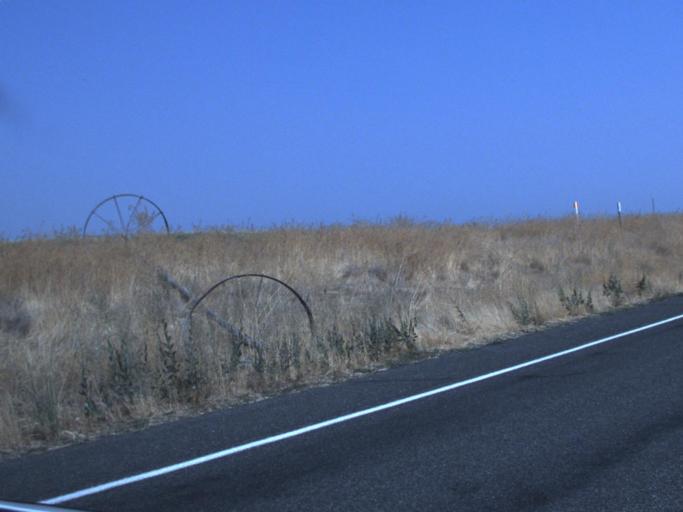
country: US
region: Washington
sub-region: Yakima County
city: Mabton
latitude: 46.2233
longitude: -120.0472
